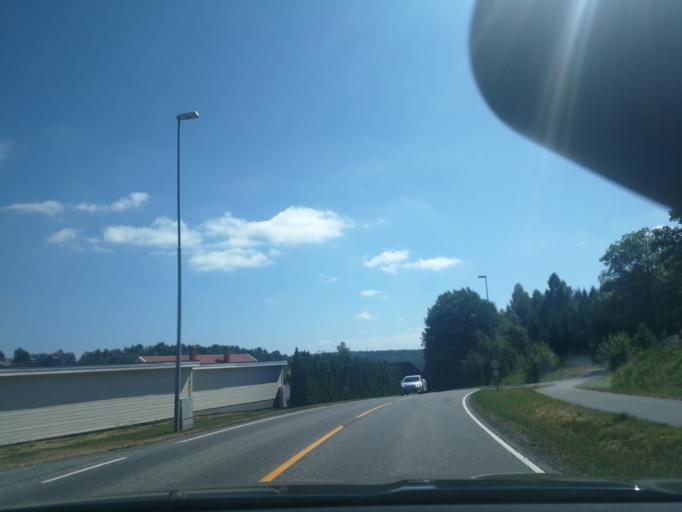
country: NO
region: Vestfold
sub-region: Stokke
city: Melsomvik
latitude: 59.2292
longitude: 10.3224
